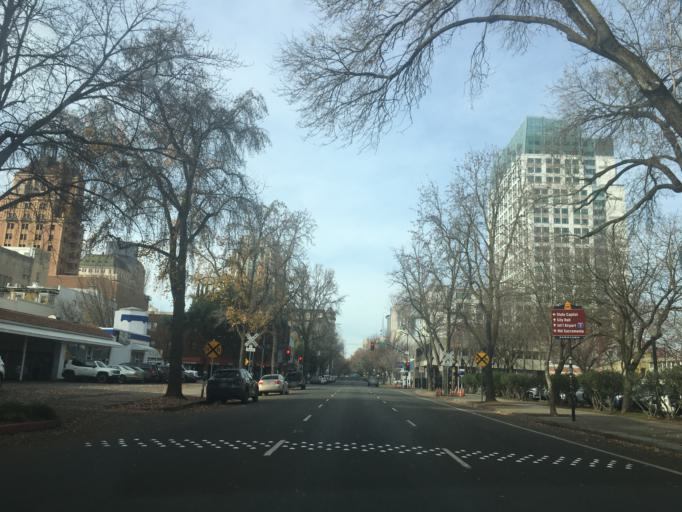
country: US
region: California
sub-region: Sacramento County
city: Sacramento
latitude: 38.5805
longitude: -121.4895
